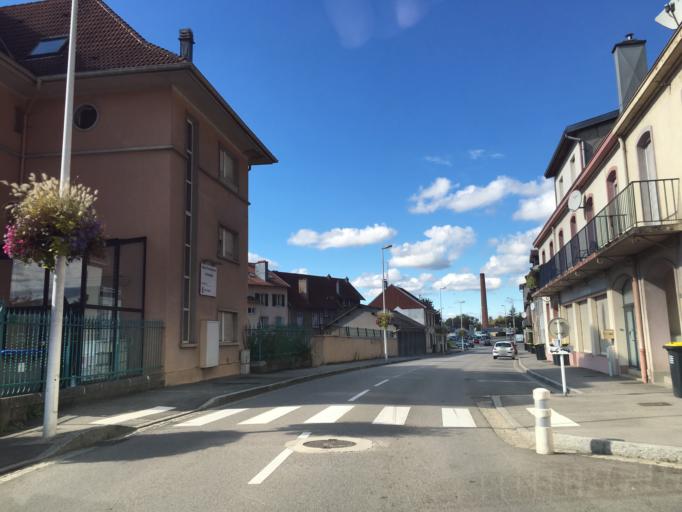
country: FR
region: Lorraine
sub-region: Departement des Vosges
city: Saint-Die-des-Vosges
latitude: 48.2908
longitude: 6.9440
